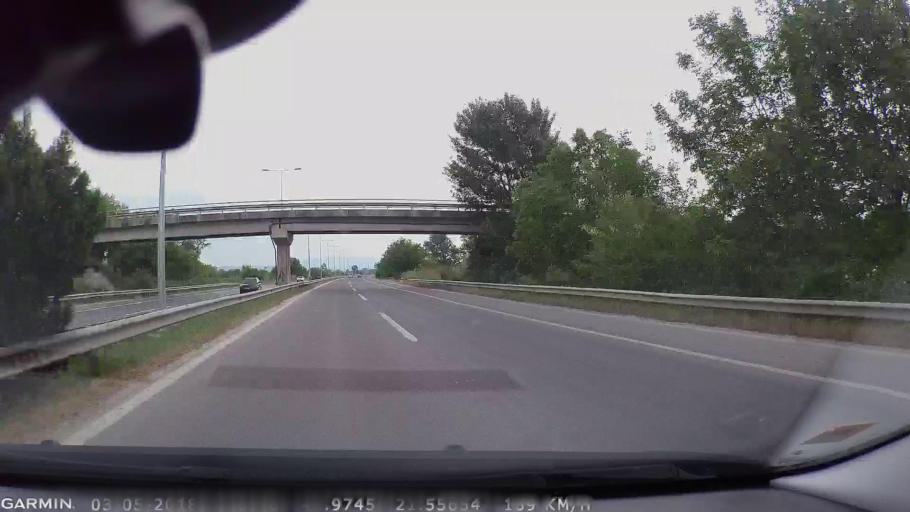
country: MK
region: Ilinden
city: Jurumleri
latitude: 41.9750
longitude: 21.5545
